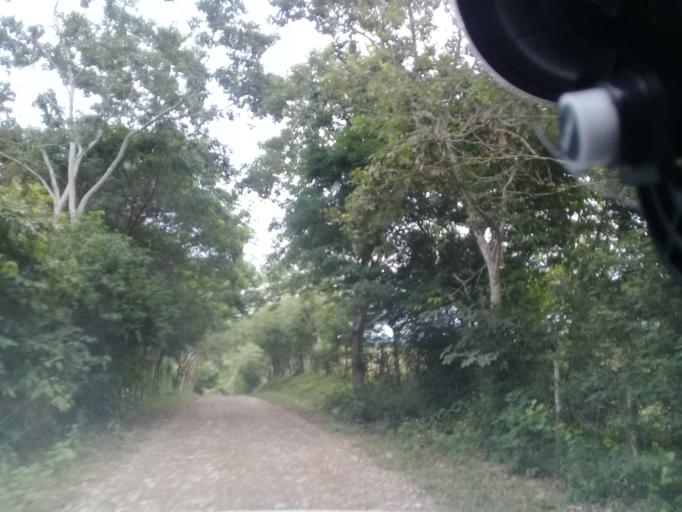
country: MX
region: Hidalgo
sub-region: Huejutla de Reyes
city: Parque de Poblamiento Solidaridad
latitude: 21.1768
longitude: -98.3772
